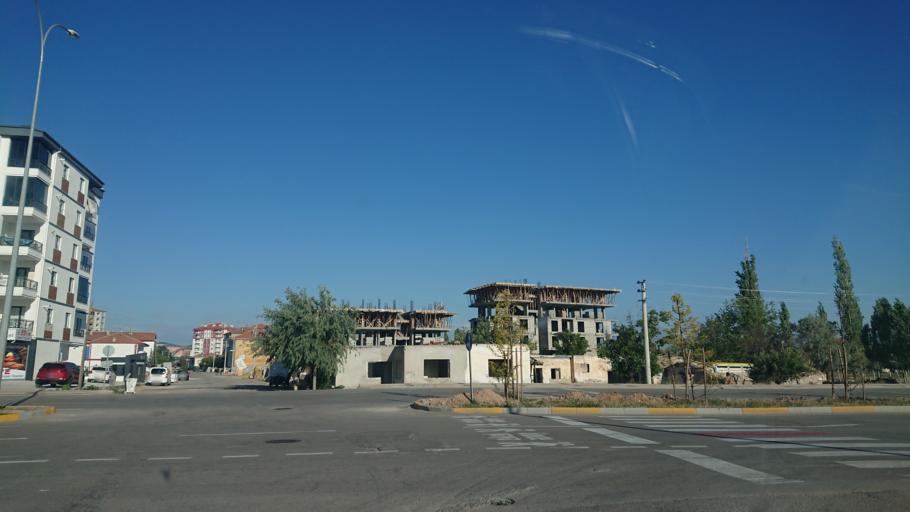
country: TR
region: Aksaray
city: Aksaray
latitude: 38.3822
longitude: 33.9918
